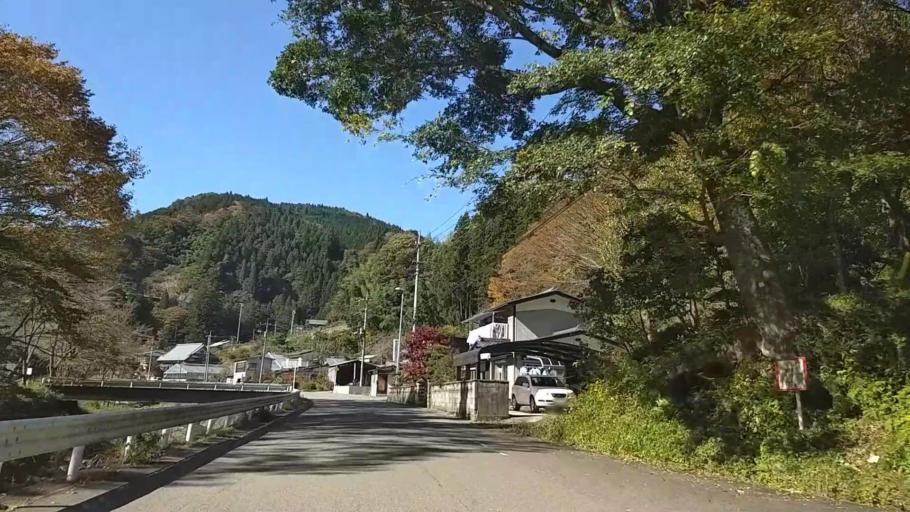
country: JP
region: Yamanashi
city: Otsuki
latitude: 35.7083
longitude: 139.0072
